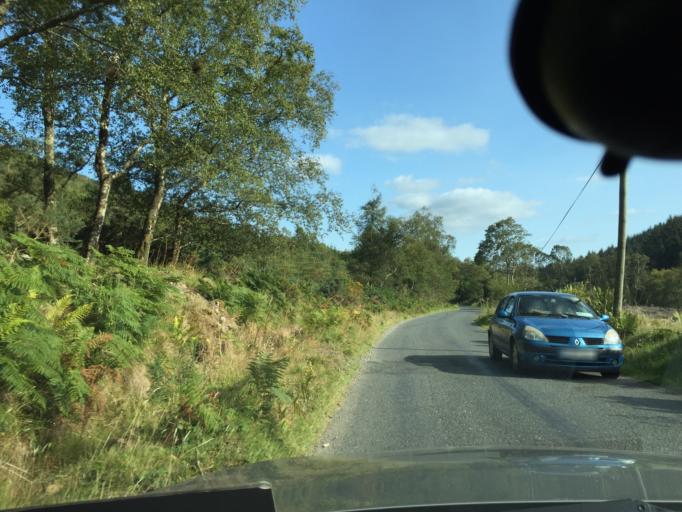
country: IE
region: Leinster
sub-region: Wicklow
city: Rathdrum
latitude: 53.0347
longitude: -6.3188
